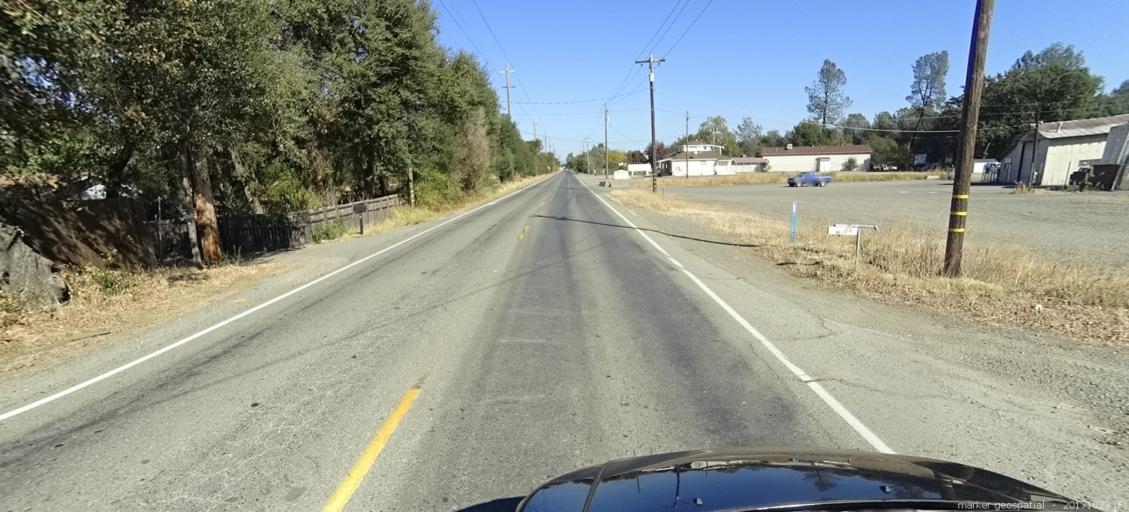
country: US
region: California
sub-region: Shasta County
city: Redding
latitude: 40.5113
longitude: -122.3880
